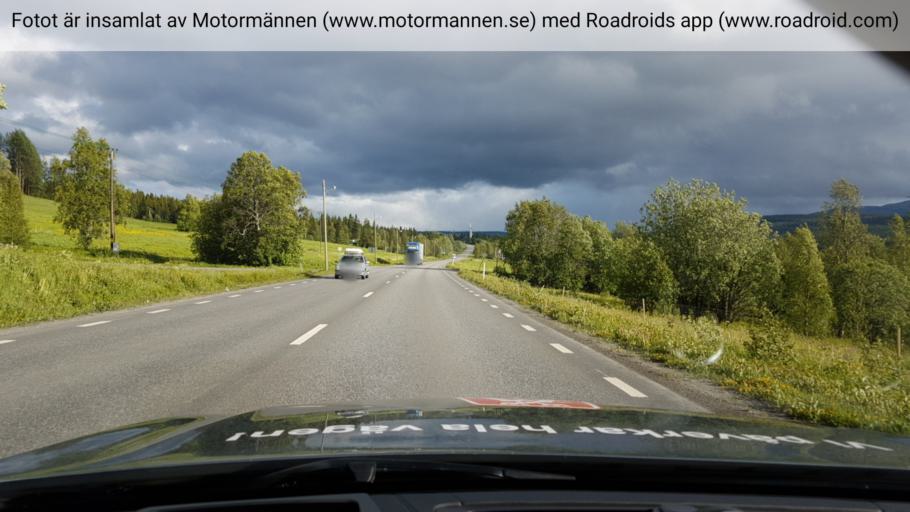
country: SE
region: Jaemtland
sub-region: Are Kommun
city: Are
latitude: 63.3555
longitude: 13.1845
